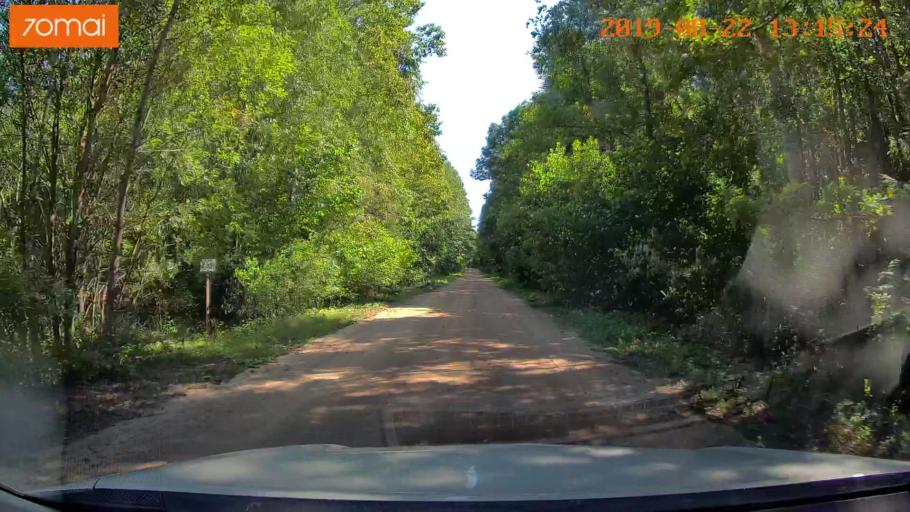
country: BY
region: Minsk
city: Prawdzinski
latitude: 53.2603
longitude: 27.8962
